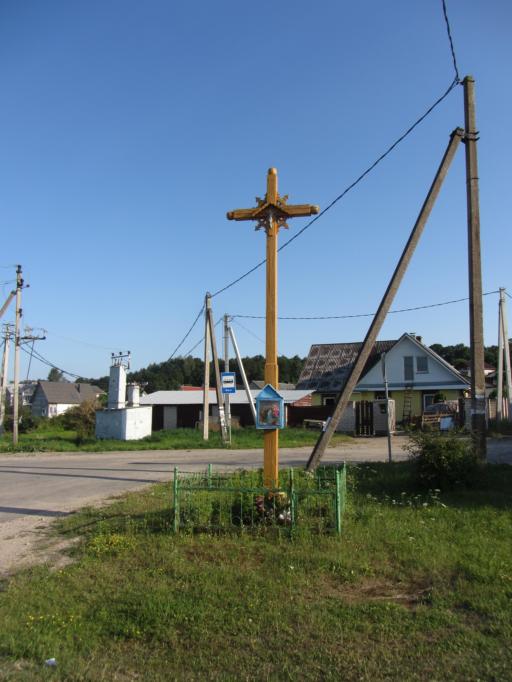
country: LT
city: Baltoji Voke
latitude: 54.5960
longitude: 25.1754
